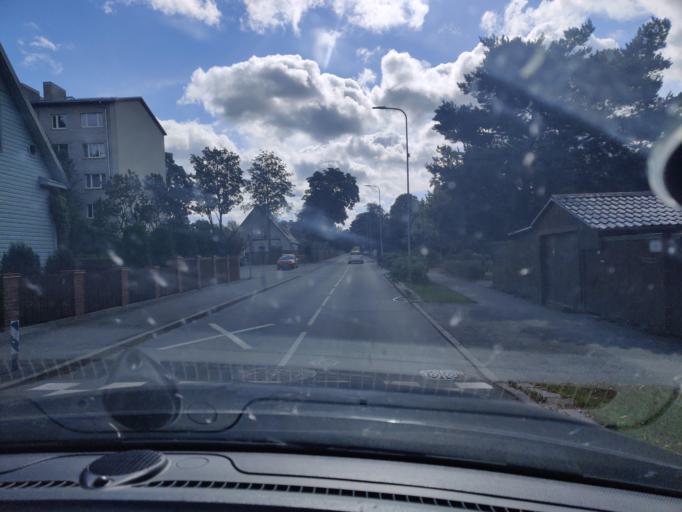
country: EE
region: Harju
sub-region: Tallinna linn
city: Tallinn
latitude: 59.4171
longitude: 24.7236
